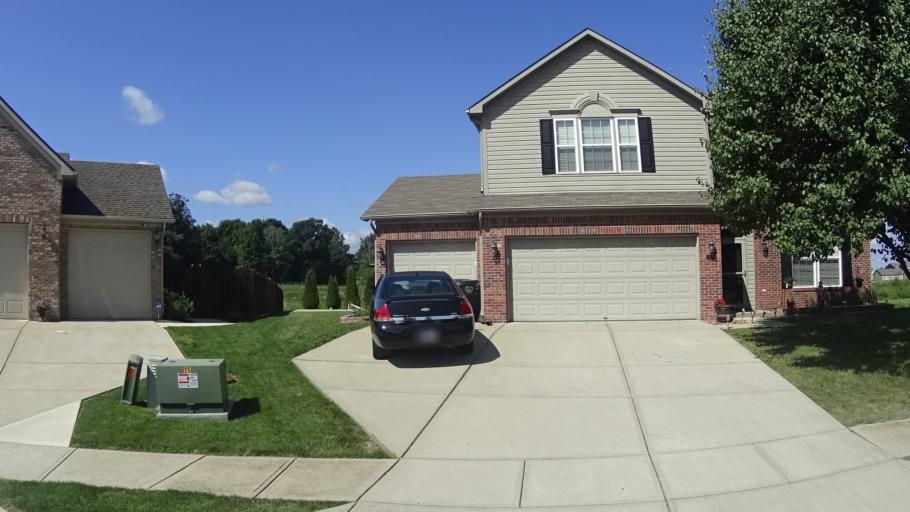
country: US
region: Indiana
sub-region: Madison County
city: Pendleton
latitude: 39.9794
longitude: -85.7439
